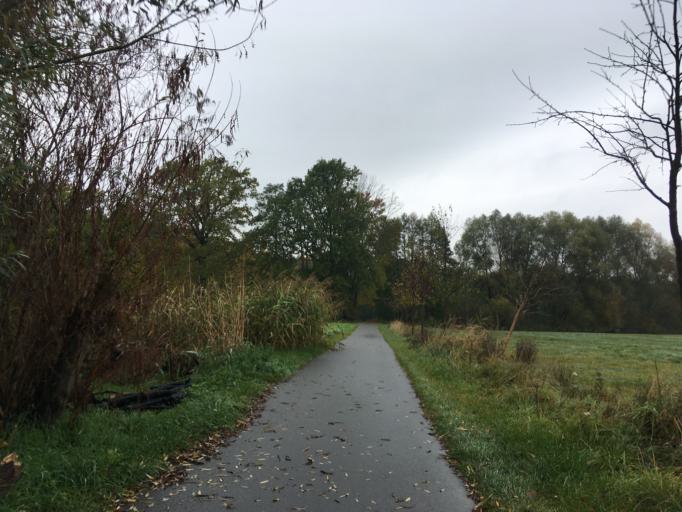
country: DE
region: Brandenburg
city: Friedland
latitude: 52.0284
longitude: 14.1743
